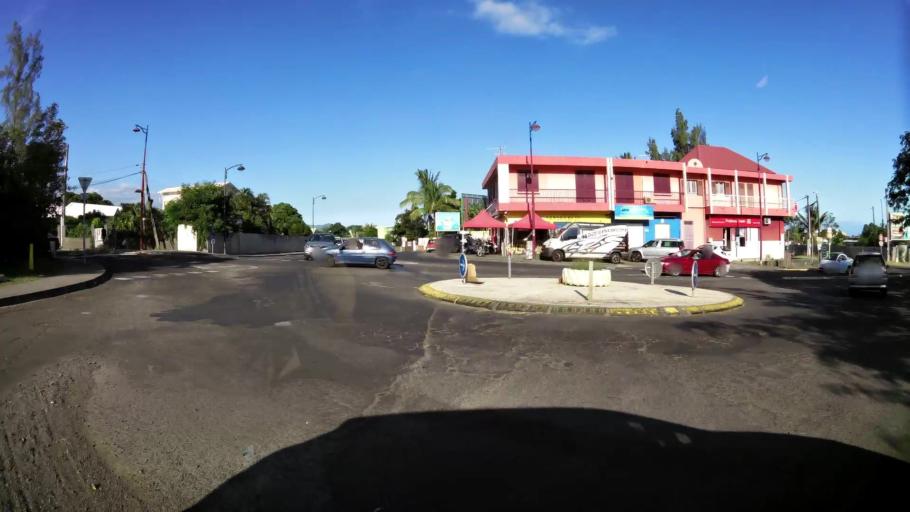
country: RE
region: Reunion
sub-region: Reunion
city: Saint-Louis
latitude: -21.2820
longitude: 55.4021
